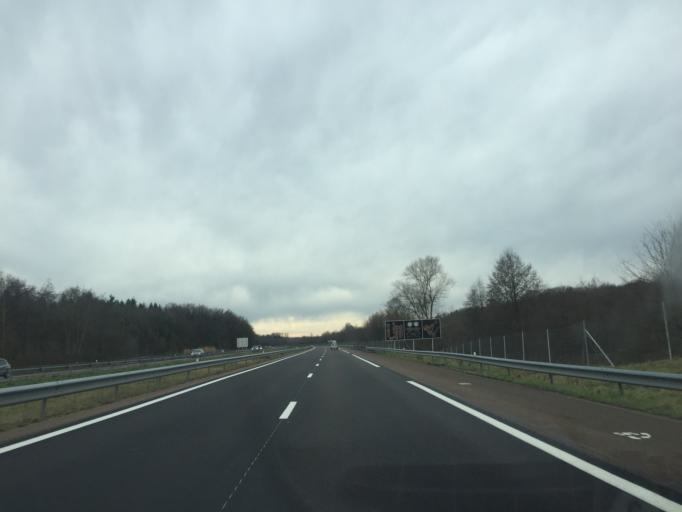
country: FR
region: Franche-Comte
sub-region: Departement du Jura
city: Bletterans
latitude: 46.8208
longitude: 5.5404
